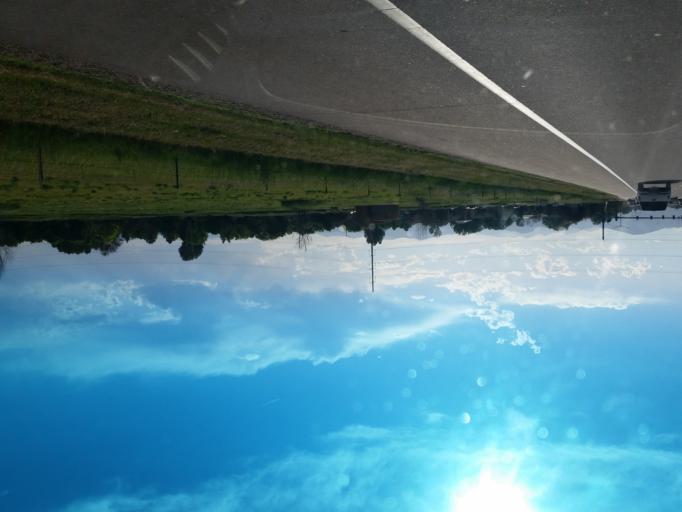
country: US
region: Colorado
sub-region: Larimer County
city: Loveland
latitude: 40.4075
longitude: -105.0415
